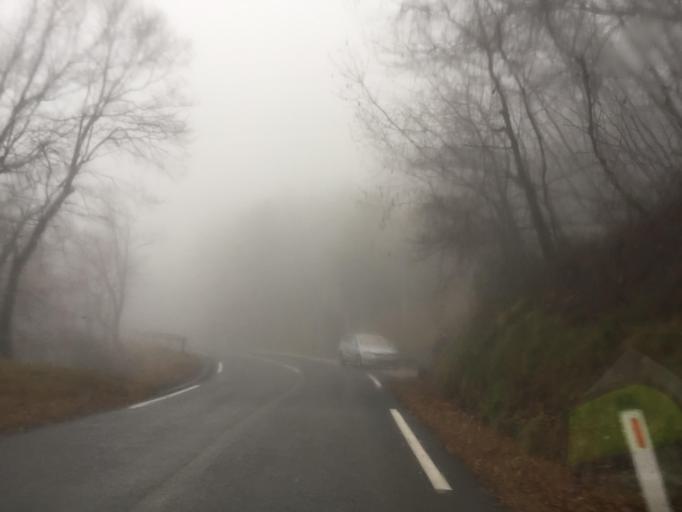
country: SI
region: Ajdovscina
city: Lokavec
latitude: 45.9334
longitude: 13.8771
